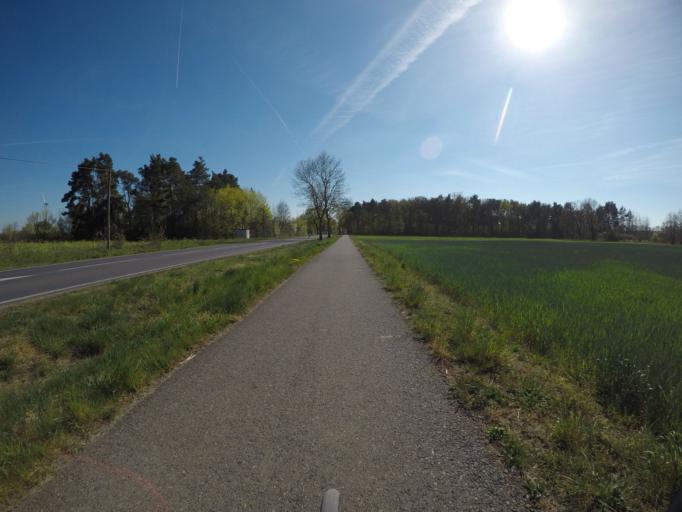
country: DE
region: Brandenburg
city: Rehfelde
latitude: 52.4957
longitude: 13.9193
